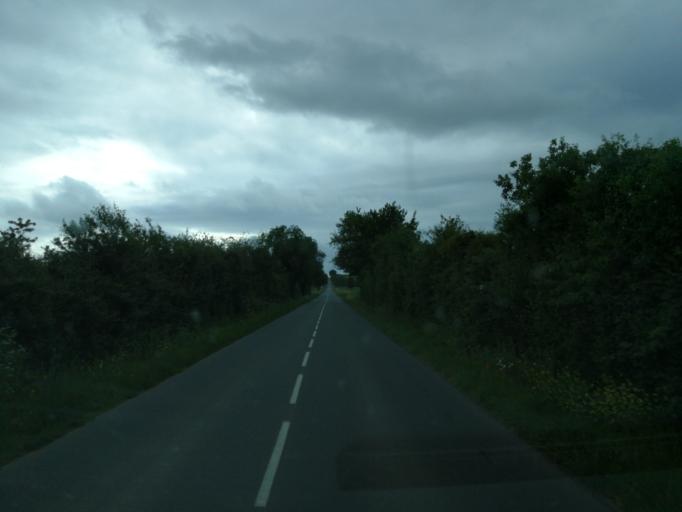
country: FR
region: Pays de la Loire
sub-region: Departement de la Vendee
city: Vix
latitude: 46.3720
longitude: -0.8926
